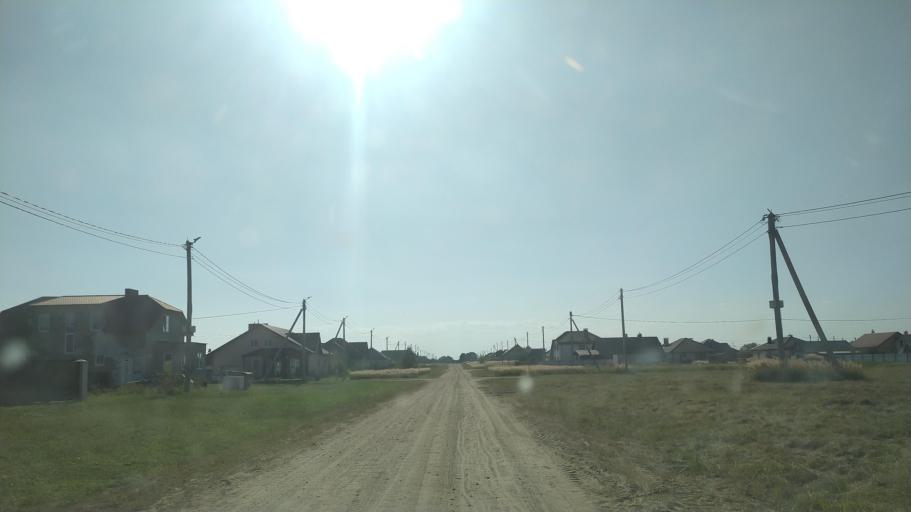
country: BY
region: Brest
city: Byaroza
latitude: 52.5157
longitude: 24.9784
